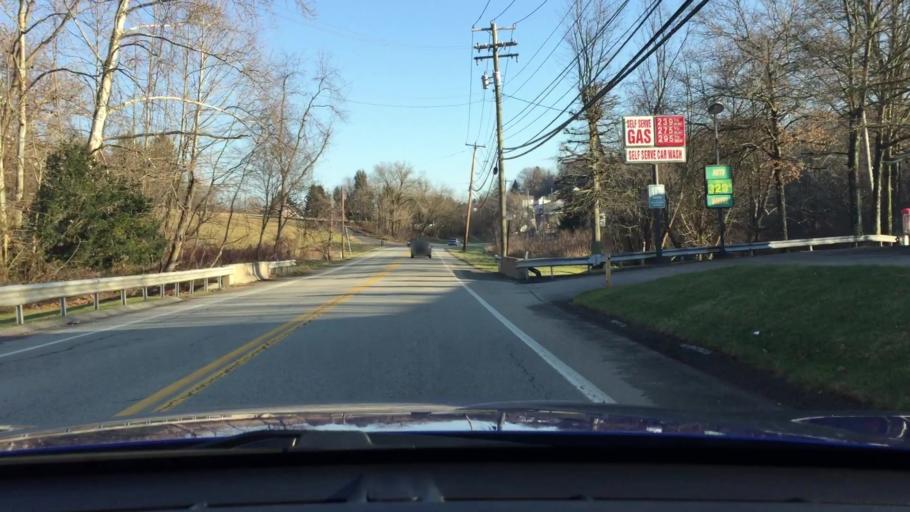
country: US
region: Pennsylvania
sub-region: Westmoreland County
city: Murrysville
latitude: 40.4206
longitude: -79.6351
